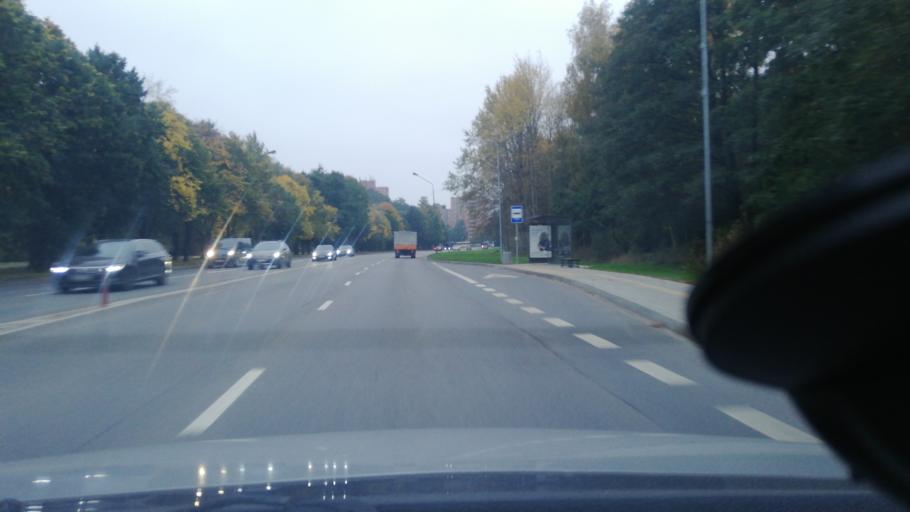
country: LT
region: Klaipedos apskritis
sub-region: Klaipeda
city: Klaipeda
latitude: 55.7370
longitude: 21.1296
